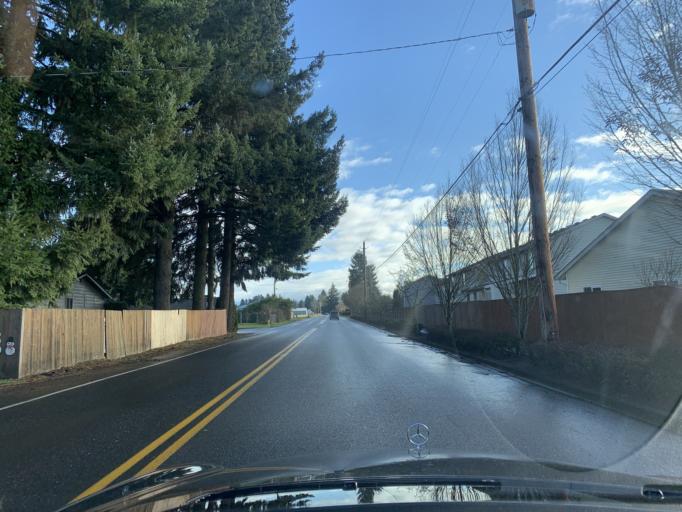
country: US
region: Washington
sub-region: Clark County
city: Five Corners
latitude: 45.6861
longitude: -122.5816
